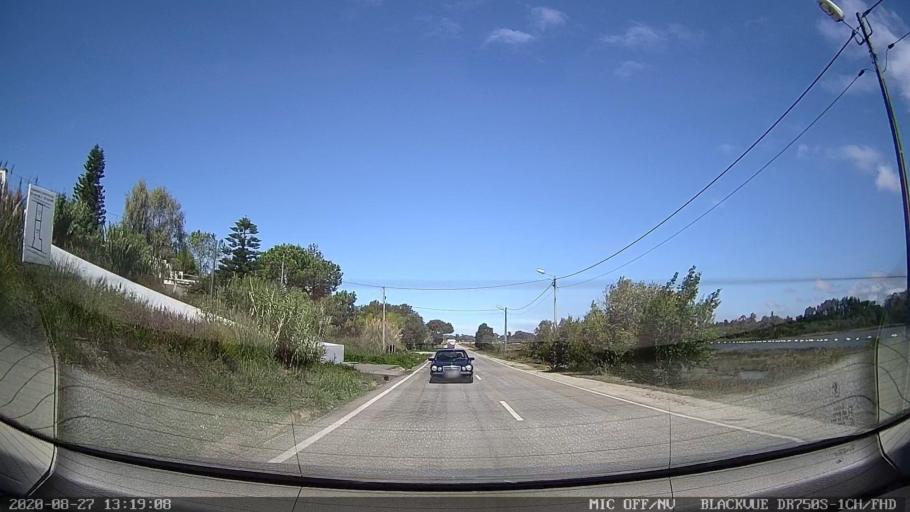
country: PT
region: Aveiro
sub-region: Vagos
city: Vagos
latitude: 40.5674
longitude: -8.6823
